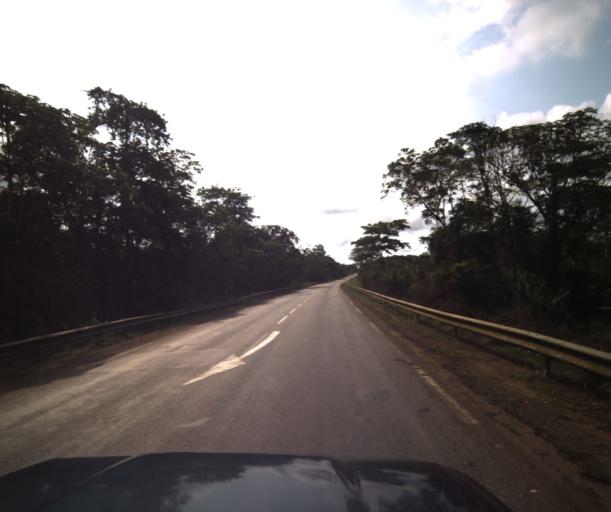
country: CM
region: Littoral
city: Edea
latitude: 3.9444
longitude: 10.0442
